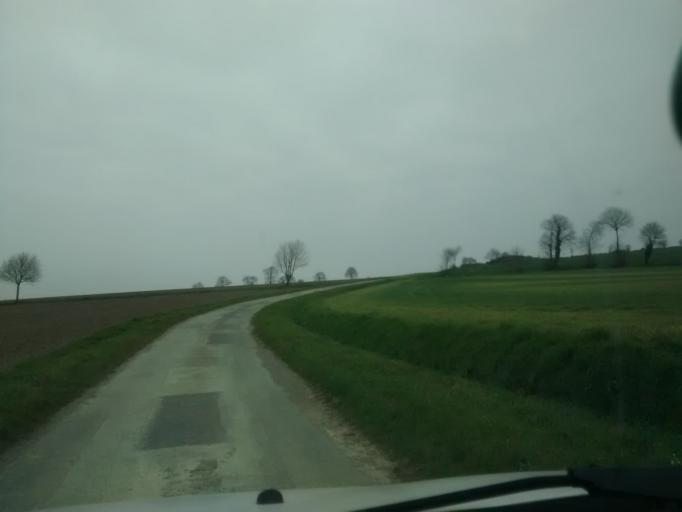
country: FR
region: Brittany
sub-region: Departement d'Ille-et-Vilaine
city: Bazouges-la-Perouse
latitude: 48.3884
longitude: -1.5956
